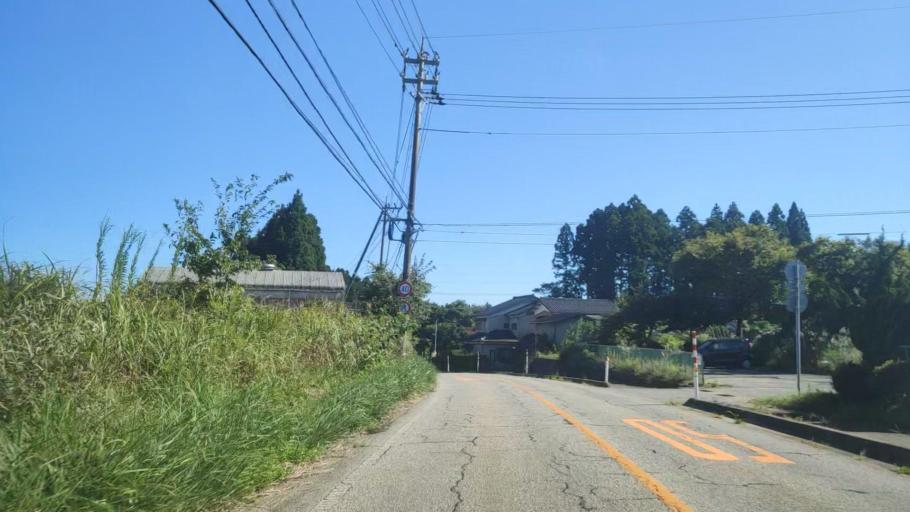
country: JP
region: Ishikawa
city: Nanao
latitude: 37.3440
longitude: 137.2283
